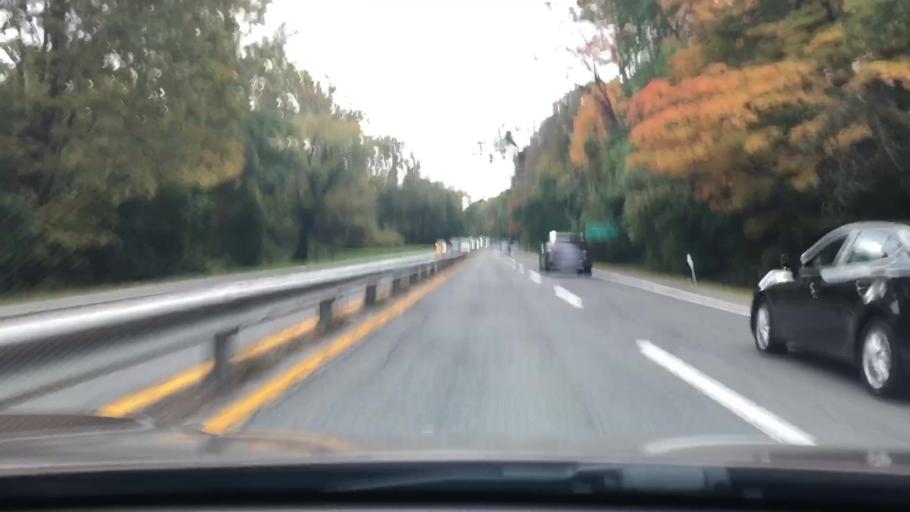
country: US
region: New York
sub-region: Westchester County
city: Tuckahoe
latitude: 40.9671
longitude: -73.8182
